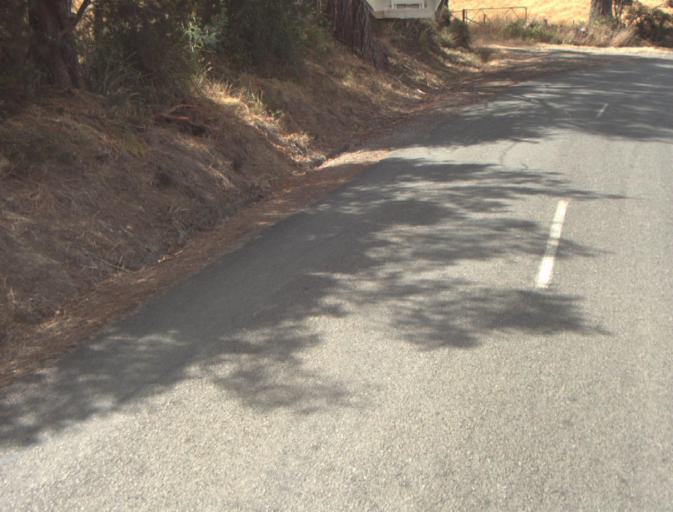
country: AU
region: Tasmania
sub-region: Launceston
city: Mayfield
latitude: -41.3110
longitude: 147.0454
